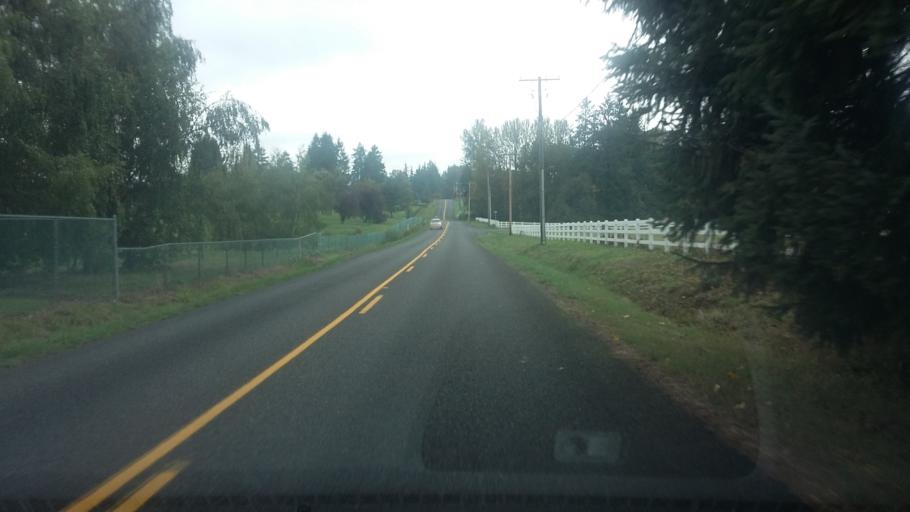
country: US
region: Washington
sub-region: Clark County
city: La Center
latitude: 45.8350
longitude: -122.6823
